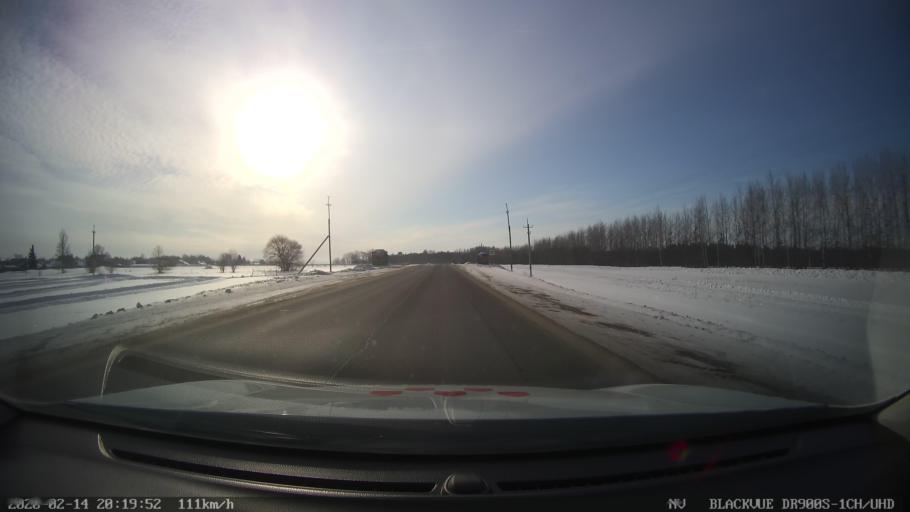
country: RU
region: Tatarstan
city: Verkhniy Uslon
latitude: 55.5644
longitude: 48.9015
